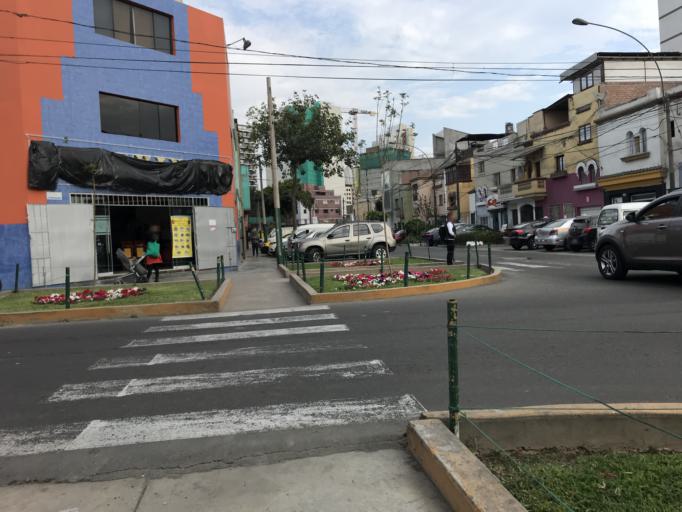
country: PE
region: Lima
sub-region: Lima
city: San Isidro
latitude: -12.0782
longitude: -77.0496
